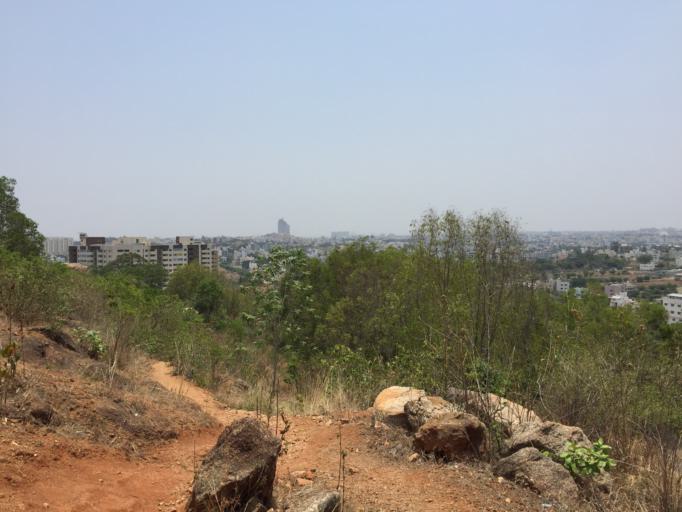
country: IN
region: Karnataka
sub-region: Bangalore Urban
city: Bangalore
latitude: 12.8898
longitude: 77.5295
